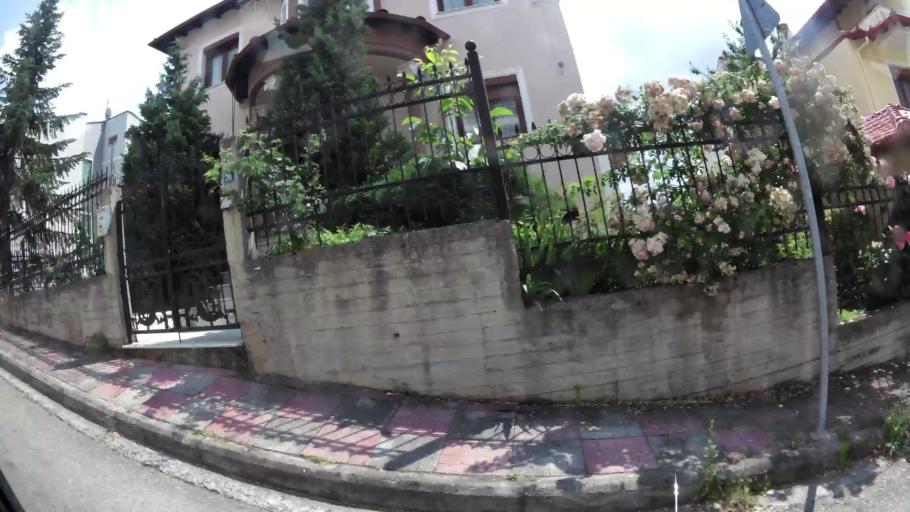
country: GR
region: West Macedonia
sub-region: Nomos Kozanis
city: Kozani
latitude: 40.3097
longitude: 21.7881
